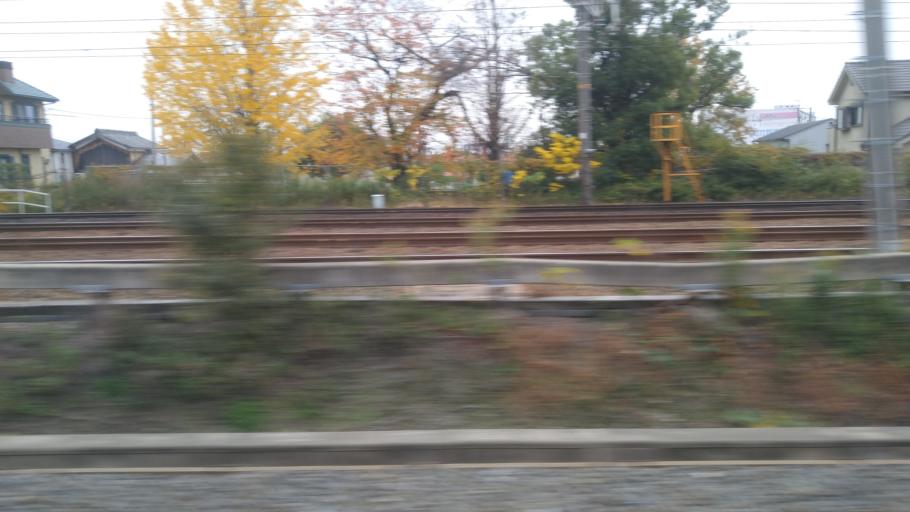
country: JP
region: Kyoto
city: Yawata
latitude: 34.8999
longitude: 135.6850
